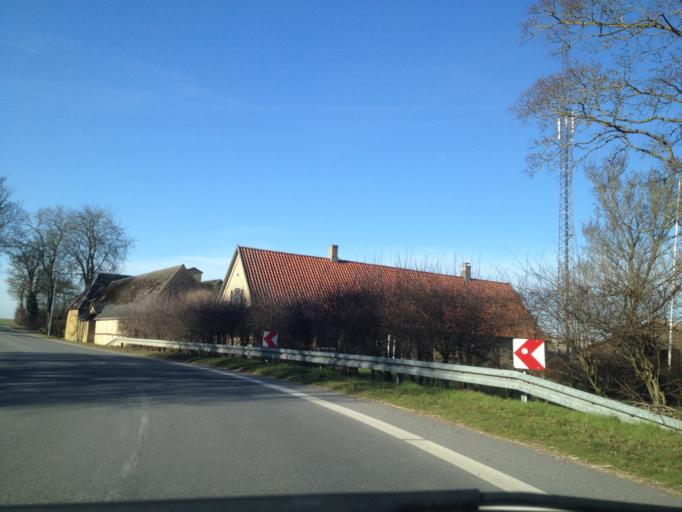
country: DK
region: South Denmark
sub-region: Kerteminde Kommune
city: Kerteminde
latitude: 55.4924
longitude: 10.6582
